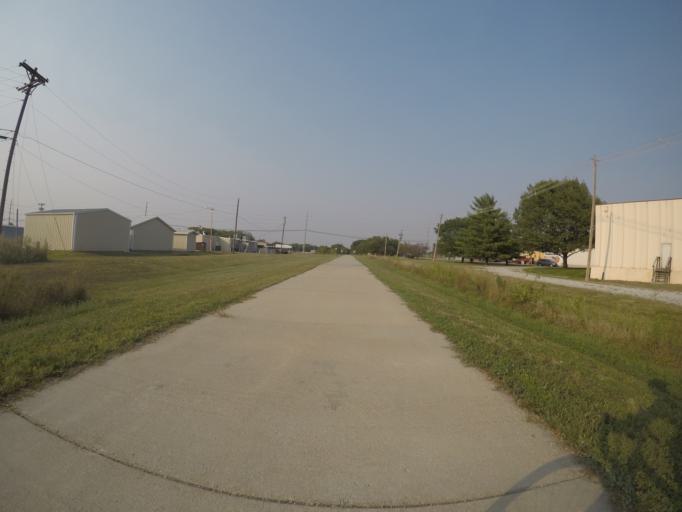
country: US
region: Nebraska
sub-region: Gage County
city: Beatrice
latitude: 40.2835
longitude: -96.7449
